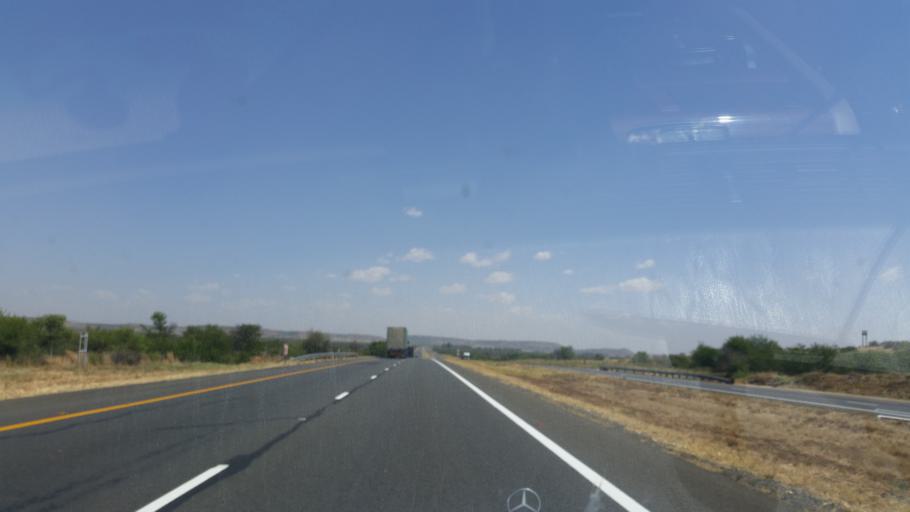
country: ZA
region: Orange Free State
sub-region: Mangaung Metropolitan Municipality
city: Bloemfontein
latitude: -28.9559
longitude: 26.3813
